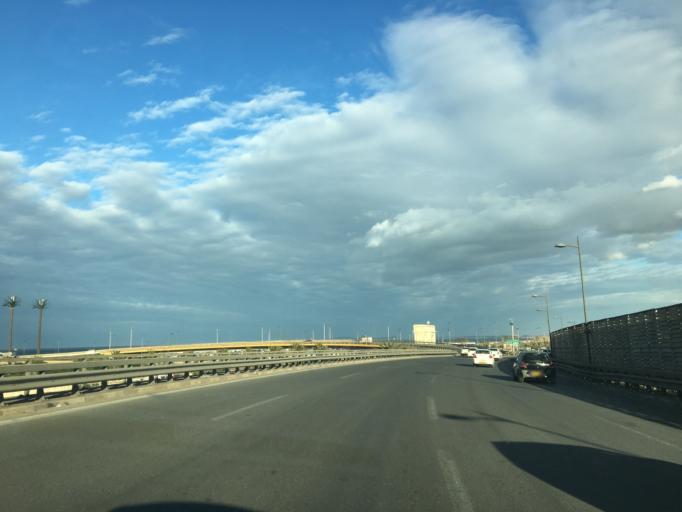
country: DZ
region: Alger
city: Bab Ezzouar
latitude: 36.7387
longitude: 3.1233
